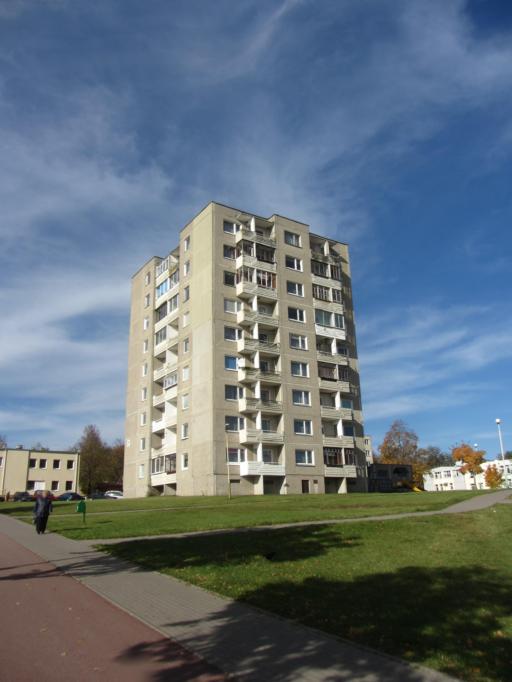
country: LT
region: Vilnius County
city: Elektrenai
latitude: 54.7847
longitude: 24.6670
